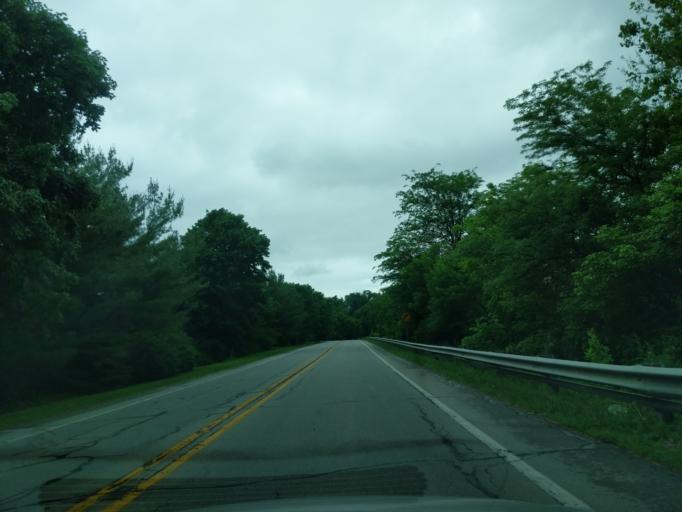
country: US
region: Indiana
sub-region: Hamilton County
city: Noblesville
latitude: 40.0544
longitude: -86.0156
